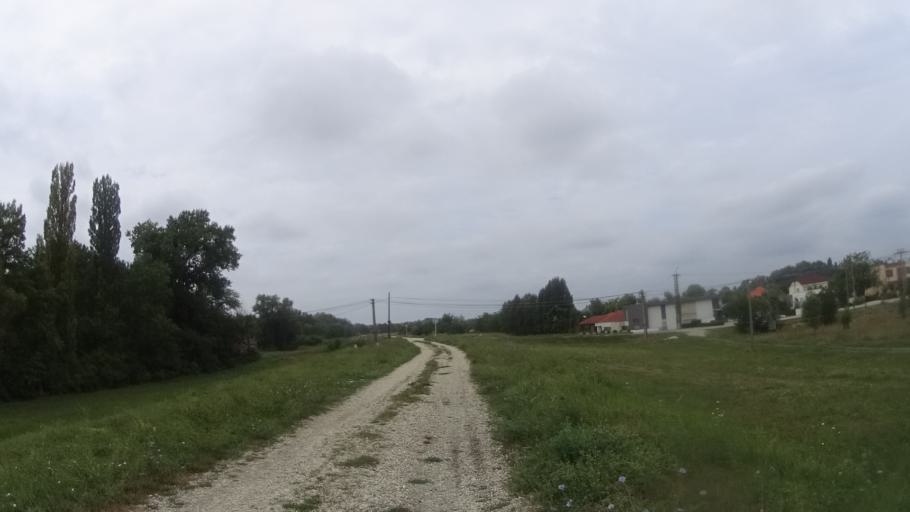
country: HU
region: Komarom-Esztergom
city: Acs
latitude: 47.7607
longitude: 18.0514
